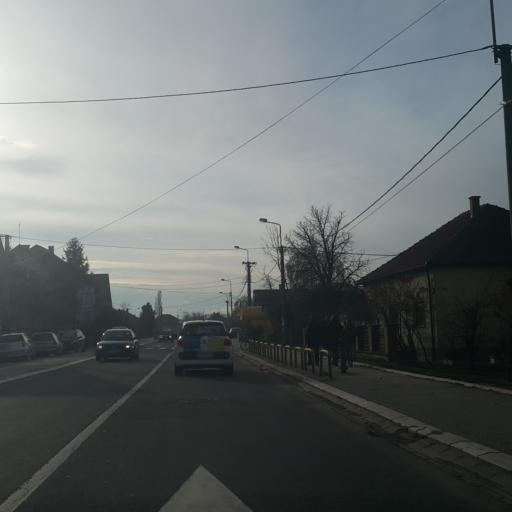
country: RS
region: Central Serbia
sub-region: Kolubarski Okrug
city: Lajkovac
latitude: 44.3662
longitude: 20.1595
